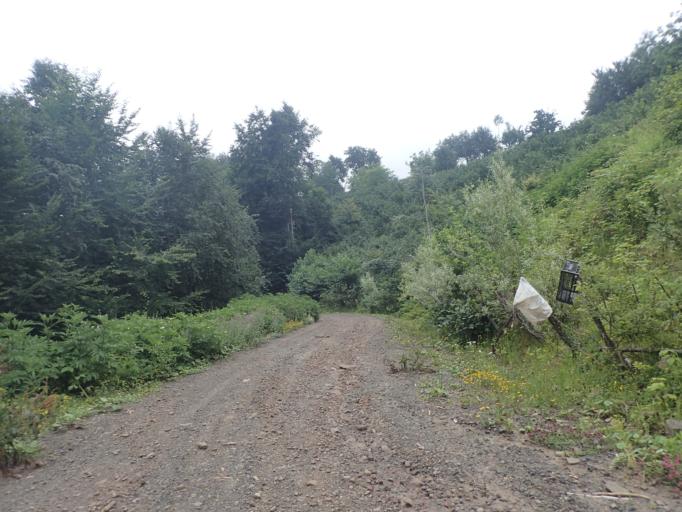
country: TR
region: Ordu
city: Akkus
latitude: 40.8882
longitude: 37.0406
